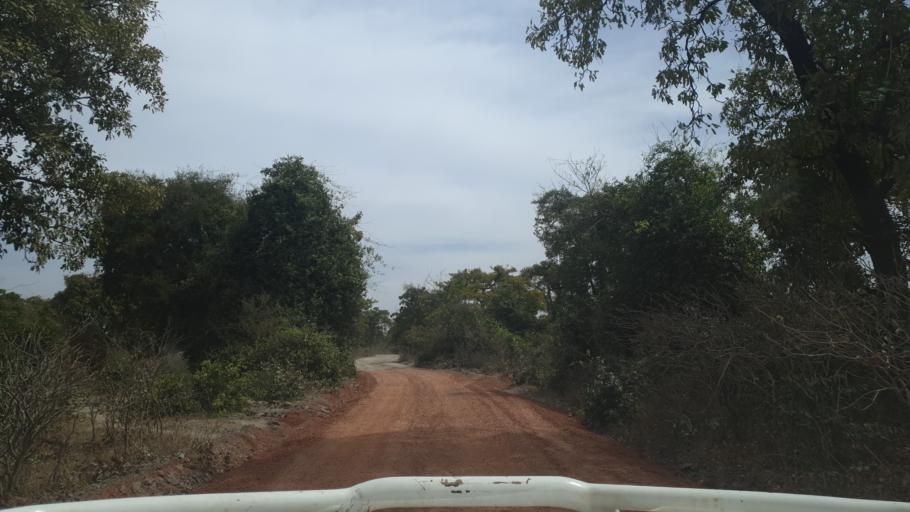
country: ML
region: Sikasso
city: Yorosso
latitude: 12.2360
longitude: -4.7429
